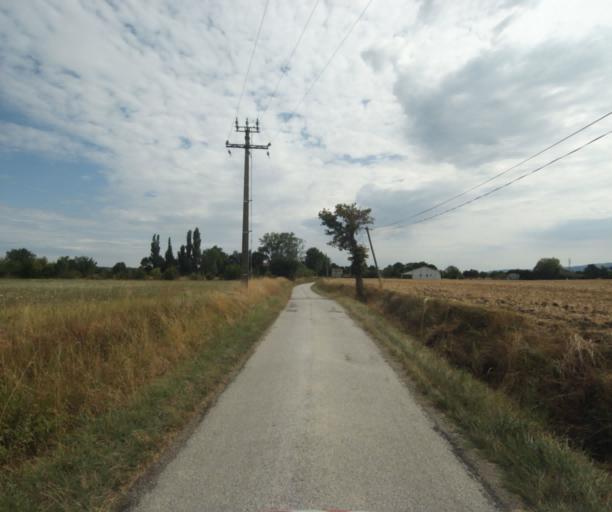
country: FR
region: Midi-Pyrenees
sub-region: Departement de la Haute-Garonne
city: Revel
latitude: 43.4500
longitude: 1.9600
